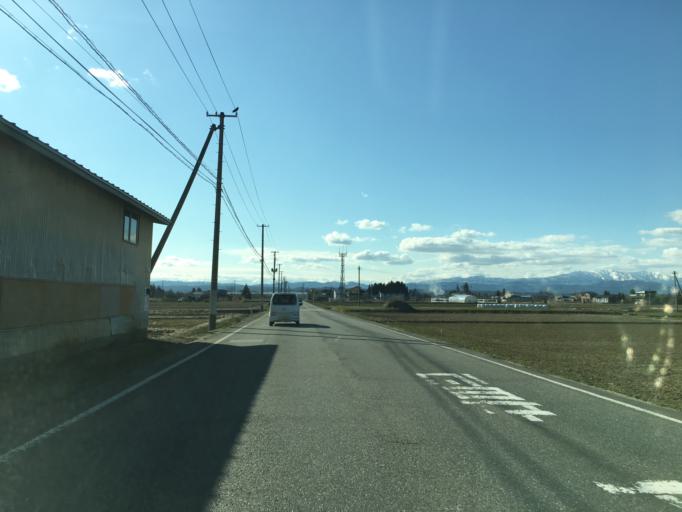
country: JP
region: Yamagata
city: Takahata
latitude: 38.0064
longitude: 140.1015
